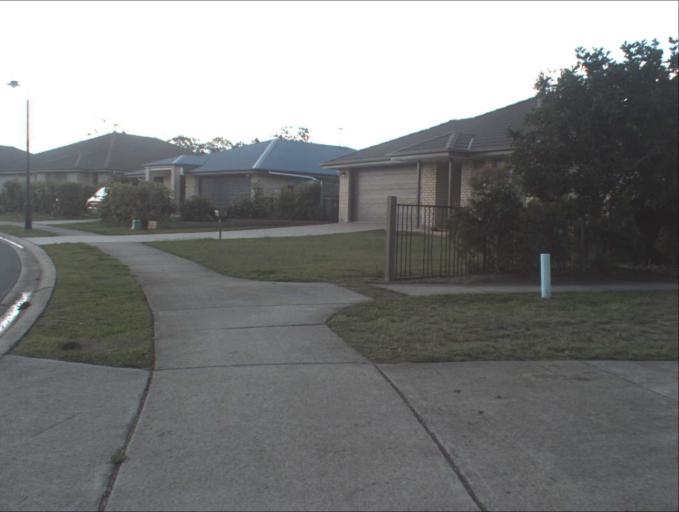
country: AU
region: Queensland
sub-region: Logan
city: North Maclean
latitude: -27.8048
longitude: 152.9599
